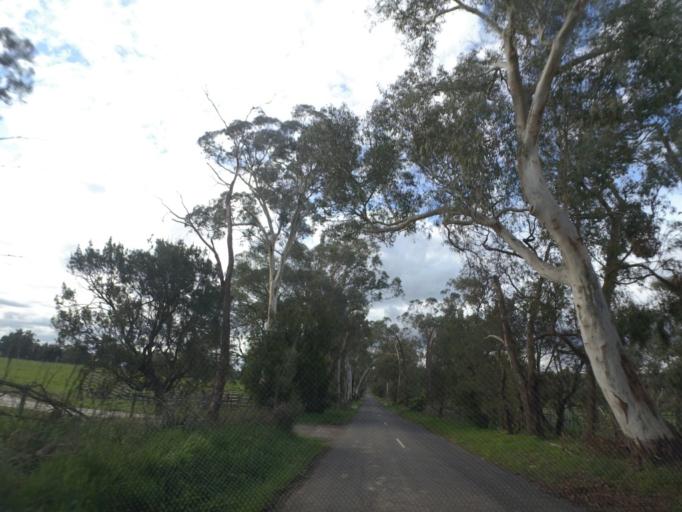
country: AU
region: Victoria
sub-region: Yarra Ranges
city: Mount Evelyn
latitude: -37.7464
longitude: 145.4119
